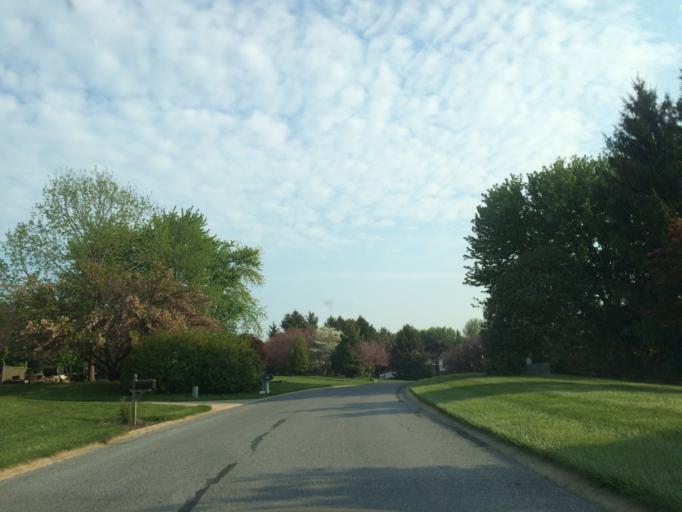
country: US
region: Maryland
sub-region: Carroll County
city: Sykesville
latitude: 39.3947
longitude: -77.0299
